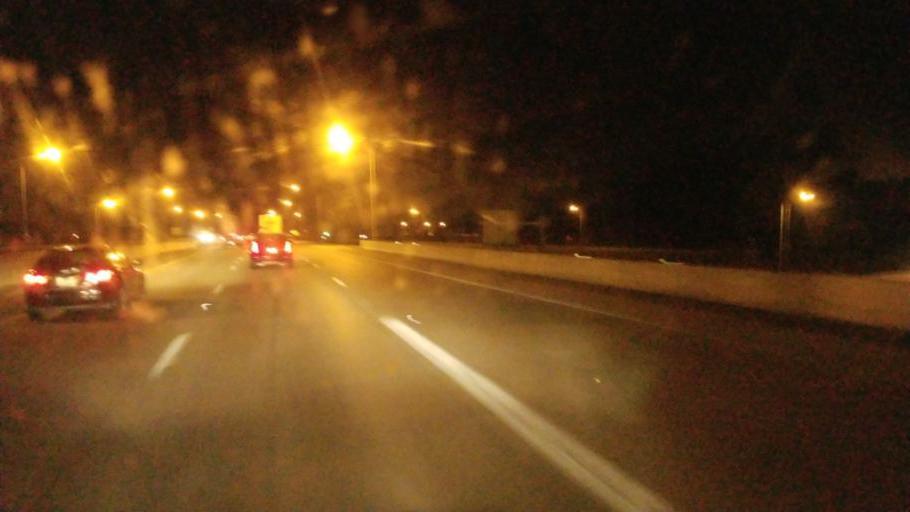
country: US
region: Indiana
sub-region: Allen County
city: Leo-Cedarville
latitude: 41.1599
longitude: -85.0634
